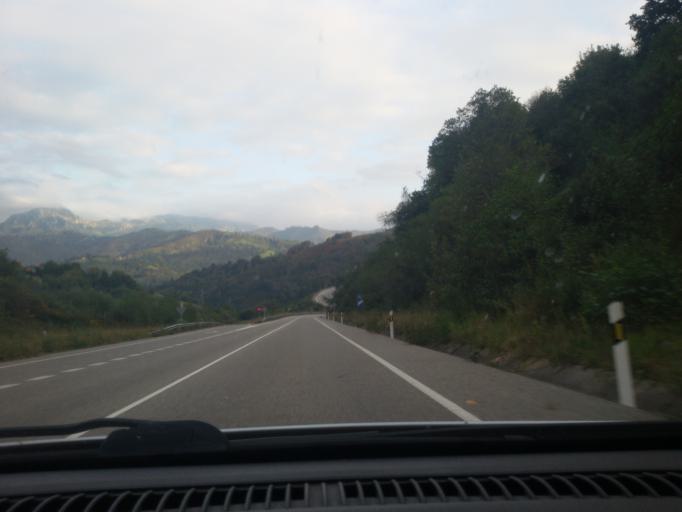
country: ES
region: Asturias
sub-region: Province of Asturias
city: Bimenes
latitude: 43.3455
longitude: -5.5846
